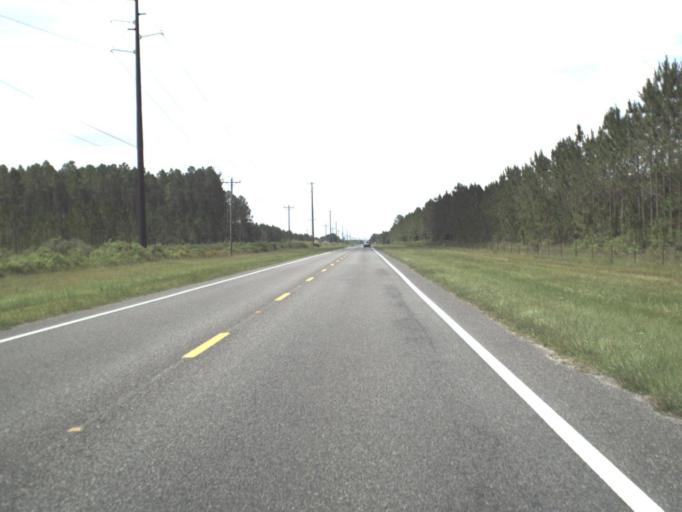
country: US
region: Florida
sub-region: Clay County
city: Middleburg
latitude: 30.0014
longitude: -81.8977
